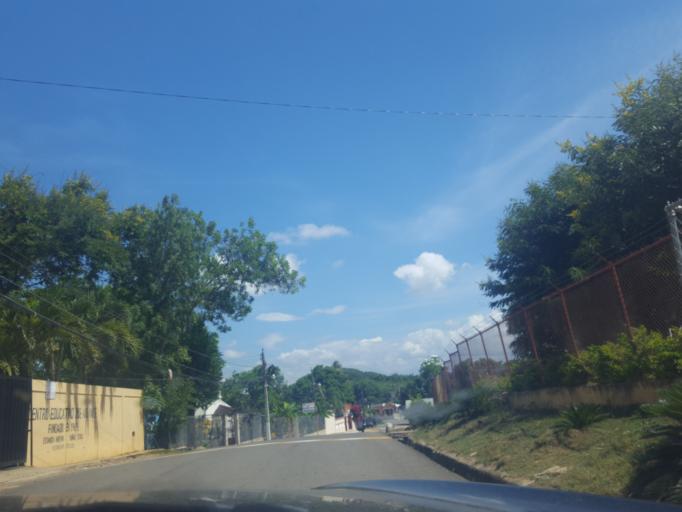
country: DO
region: Santiago
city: Baitoa
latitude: 19.3712
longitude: -70.6539
